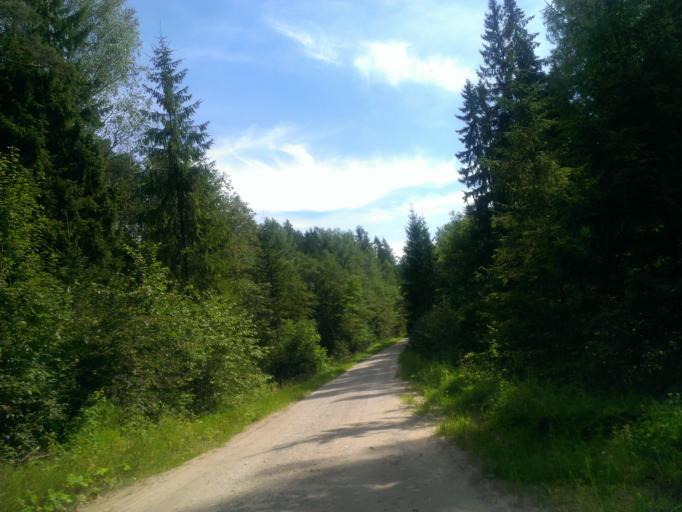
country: LV
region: Ligatne
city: Ligatne
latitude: 57.2240
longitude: 24.9755
